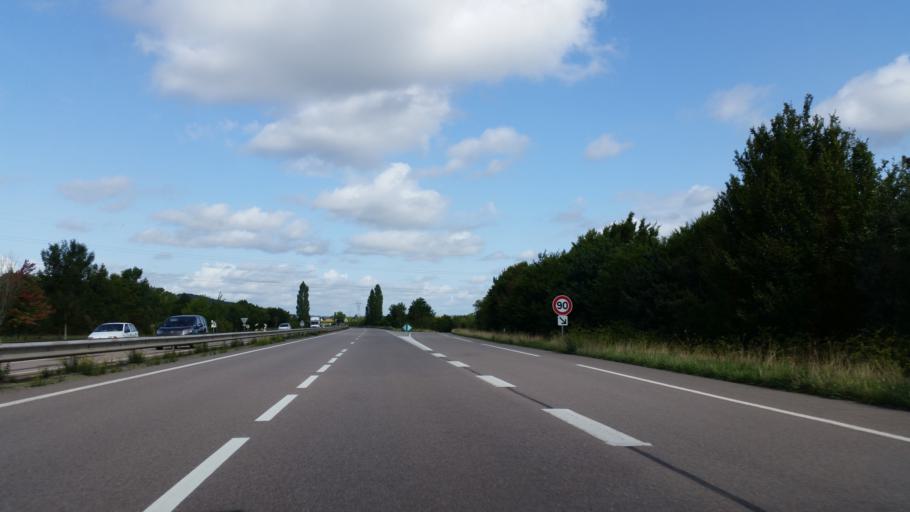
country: FR
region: Lorraine
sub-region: Departement des Vosges
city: Vincey
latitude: 48.3427
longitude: 6.3128
